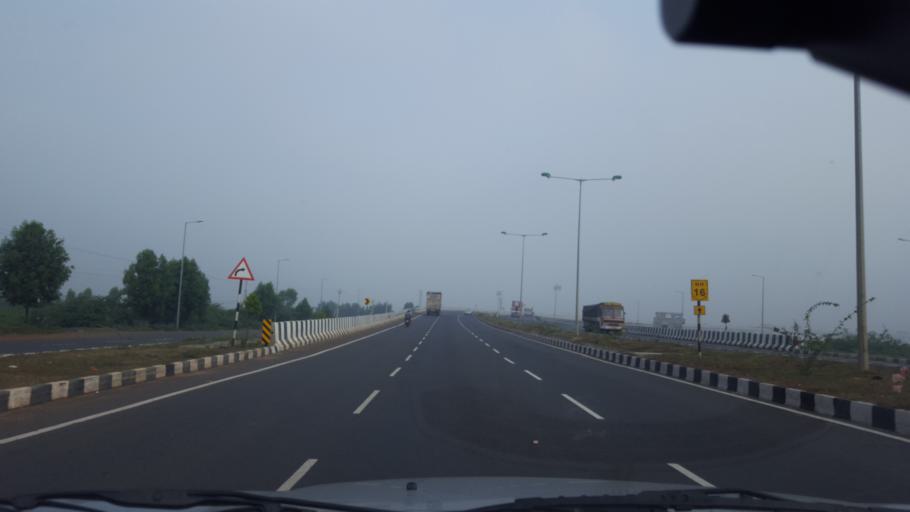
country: IN
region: Andhra Pradesh
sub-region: Prakasam
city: Ongole
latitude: 15.4667
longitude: 80.0483
